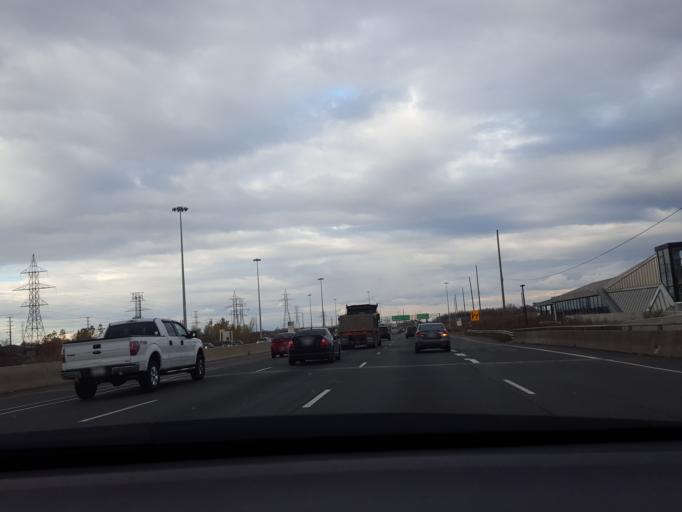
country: CA
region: Ontario
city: Mississauga
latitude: 43.6075
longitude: -79.6369
